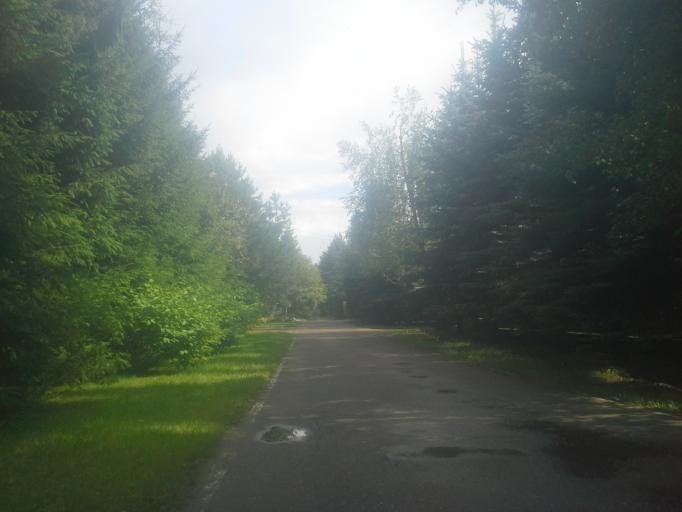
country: RU
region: Moskovskaya
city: Zhavoronki
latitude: 55.6450
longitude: 37.1412
